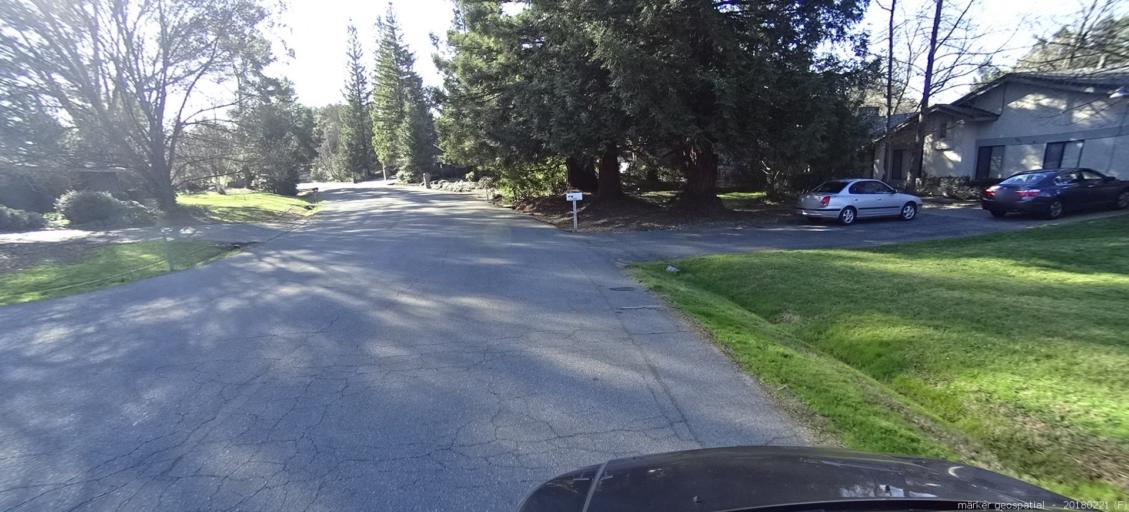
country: US
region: California
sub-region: Sacramento County
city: Orangevale
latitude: 38.6774
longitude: -121.2500
